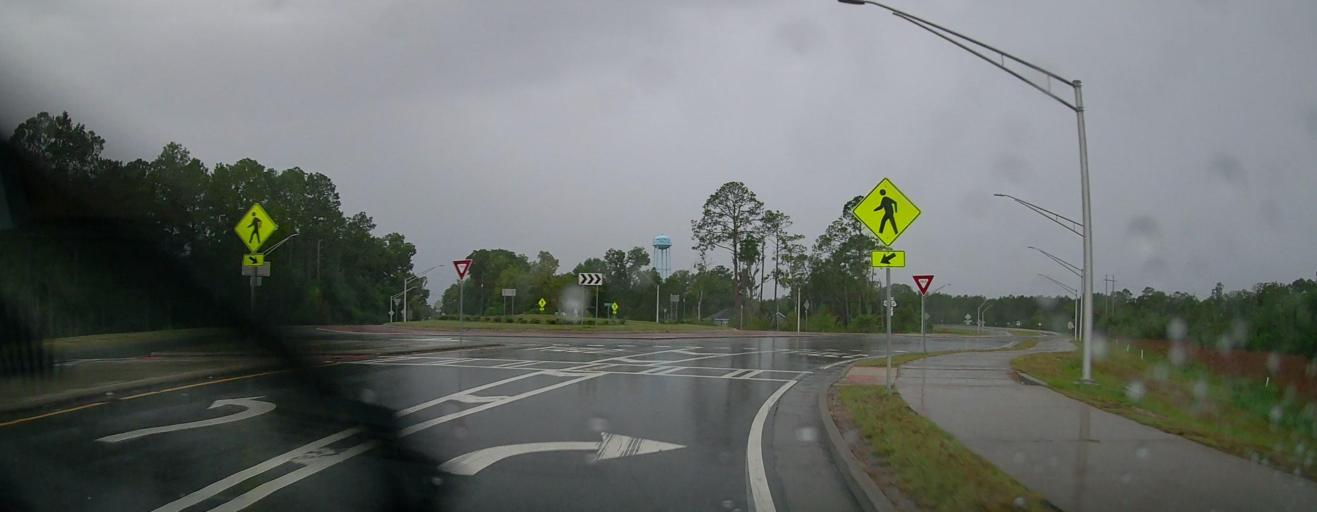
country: US
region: Georgia
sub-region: Clinch County
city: Homerville
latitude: 31.0755
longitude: -82.6449
